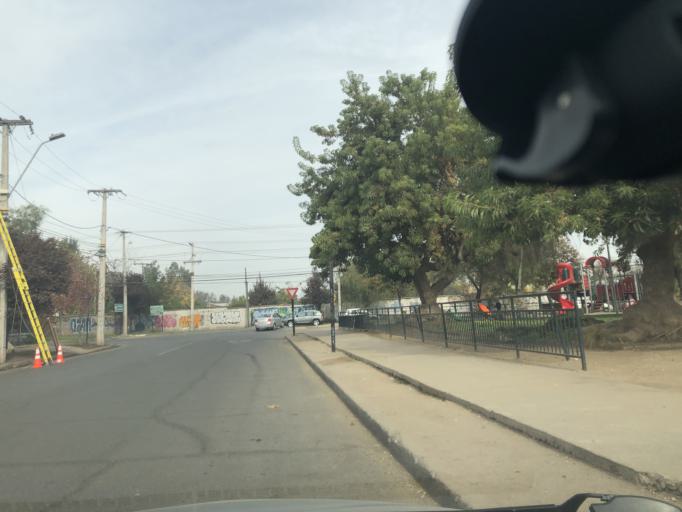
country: CL
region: Santiago Metropolitan
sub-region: Provincia de Cordillera
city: Puente Alto
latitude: -33.5797
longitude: -70.5761
